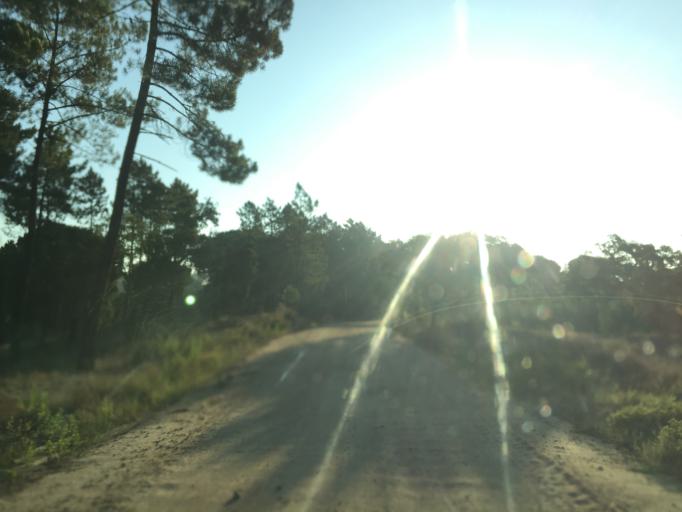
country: PT
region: Portalegre
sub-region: Ponte de Sor
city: Santo Andre
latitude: 39.0980
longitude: -8.3472
